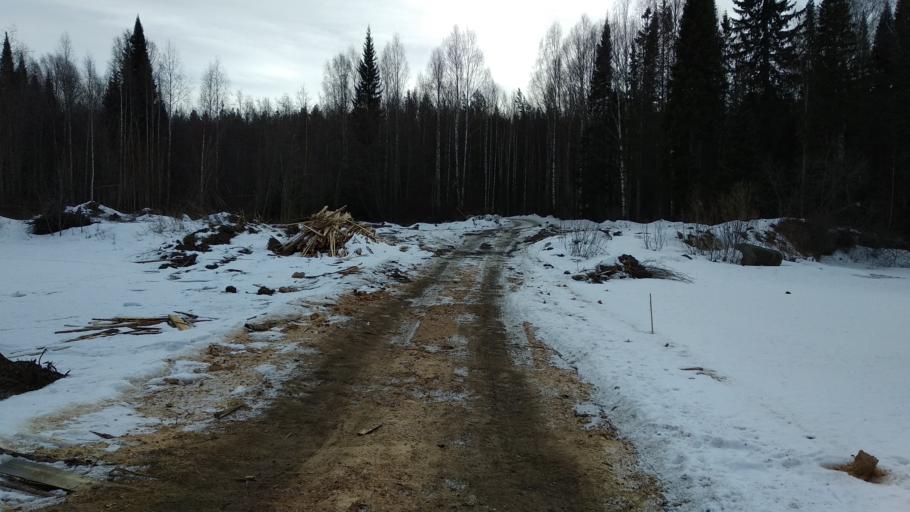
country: RU
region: Sverdlovsk
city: Severoural'sk
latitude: 60.0201
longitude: 59.7524
